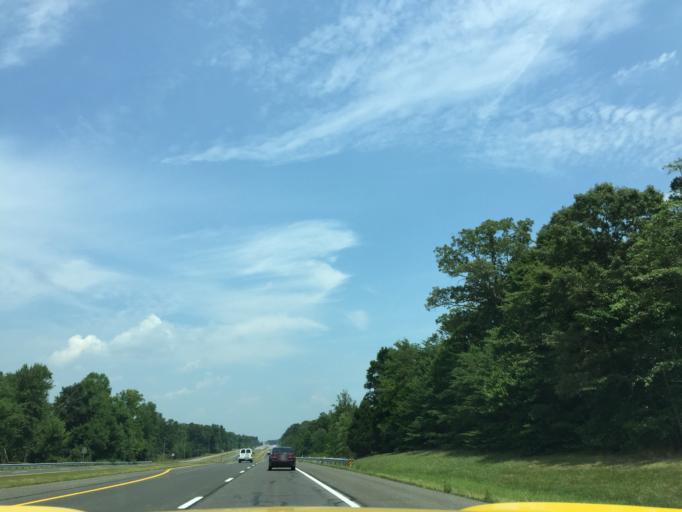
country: US
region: Maryland
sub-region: Prince George's County
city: Accokeek
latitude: 38.6566
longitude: -77.0276
